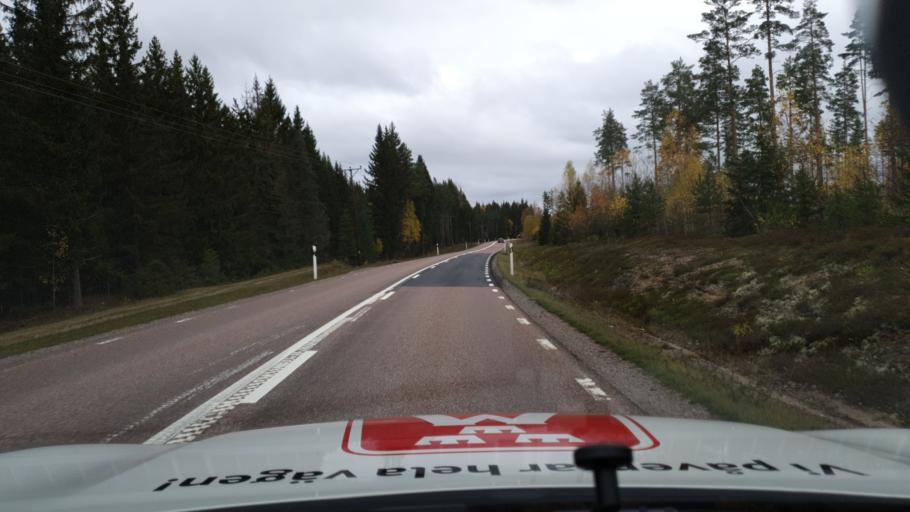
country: SE
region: Gaevleborg
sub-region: Gavle Kommun
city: Hedesunda
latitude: 60.4883
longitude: 16.9351
